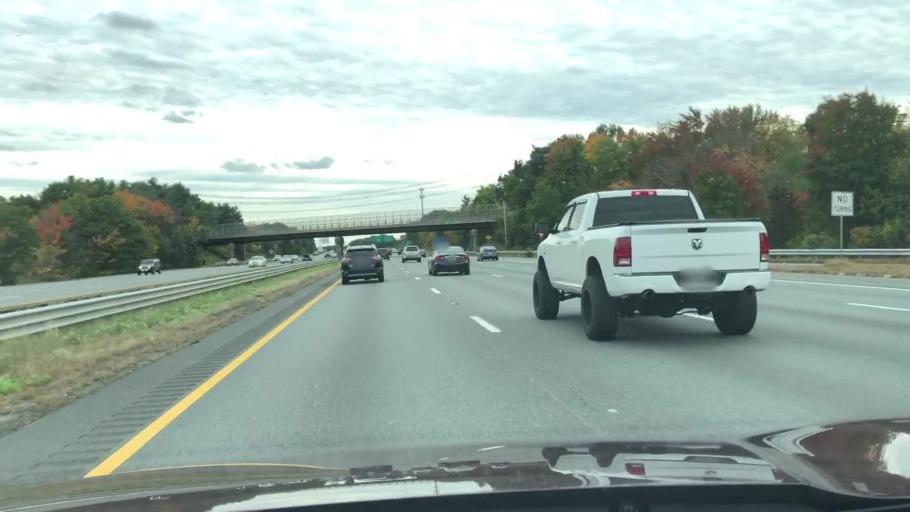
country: US
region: Massachusetts
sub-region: Middlesex County
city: Wilmington
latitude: 42.5349
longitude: -71.1355
